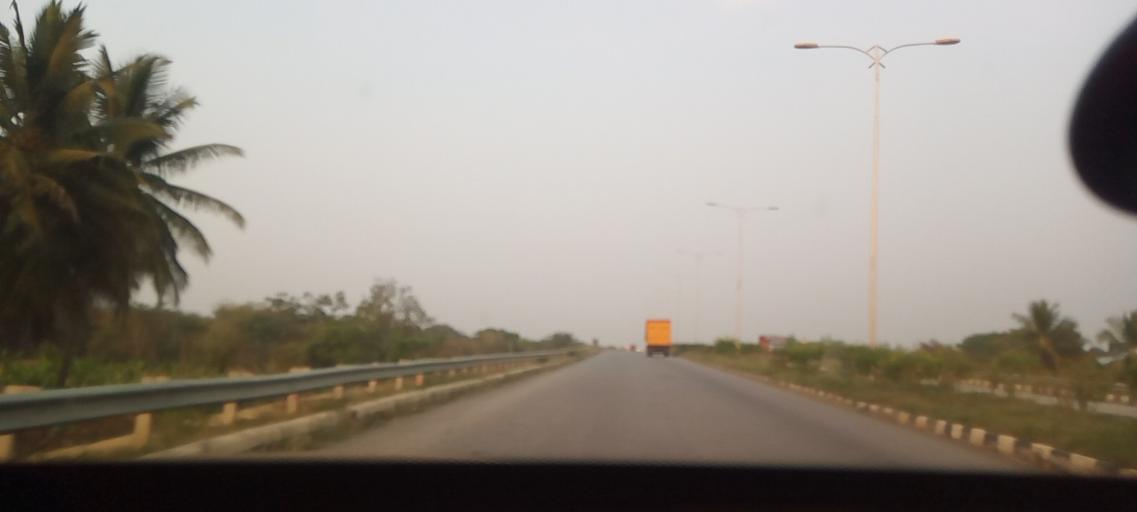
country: IN
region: Karnataka
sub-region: Tumkur
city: Kunigal
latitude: 13.0159
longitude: 77.0425
